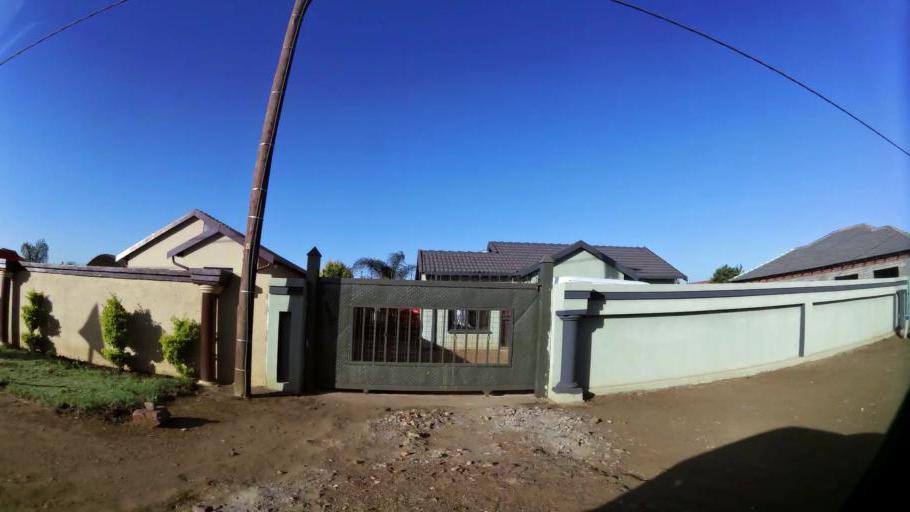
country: ZA
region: Gauteng
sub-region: City of Tshwane Metropolitan Municipality
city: Mabopane
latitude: -25.5935
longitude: 28.1117
